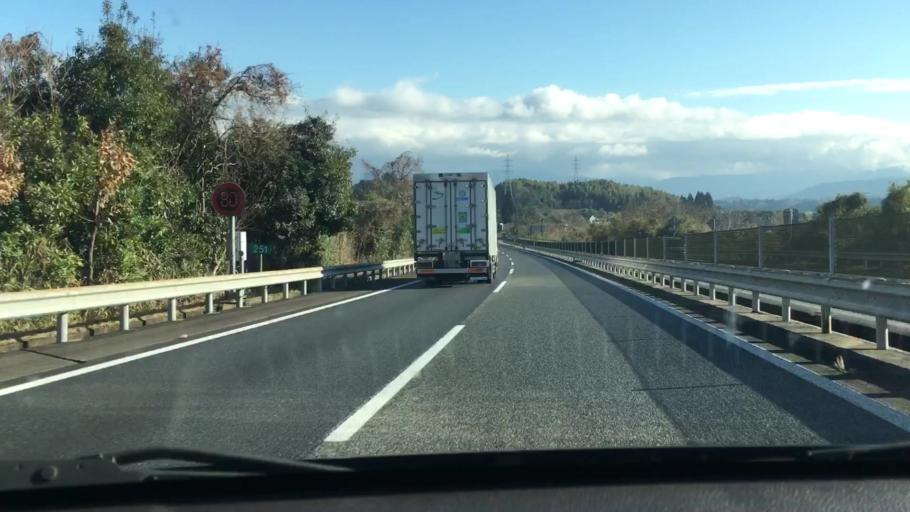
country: JP
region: Kumamoto
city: Hitoyoshi
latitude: 32.2381
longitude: 130.7619
